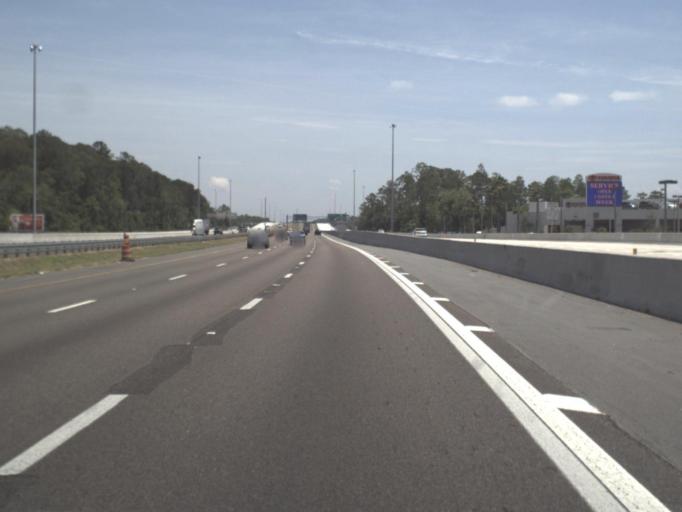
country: US
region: Florida
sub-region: Clay County
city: Bellair-Meadowbrook Terrace
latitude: 30.2006
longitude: -81.7502
